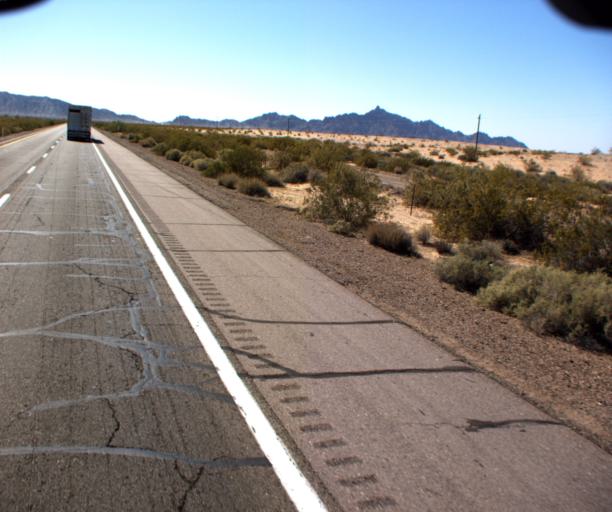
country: US
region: Arizona
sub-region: Yuma County
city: Wellton
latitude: 32.7479
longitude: -113.6698
